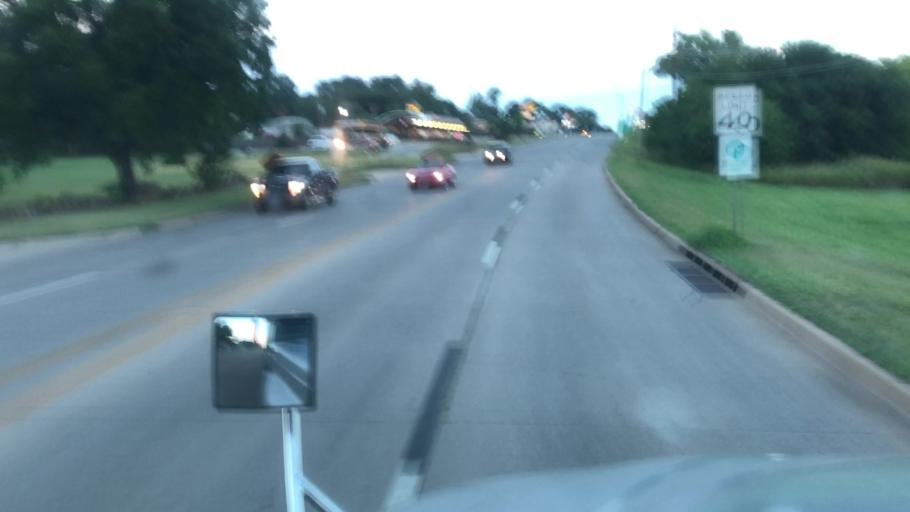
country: US
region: Oklahoma
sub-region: Kay County
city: Ponca City
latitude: 36.6963
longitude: -97.0672
